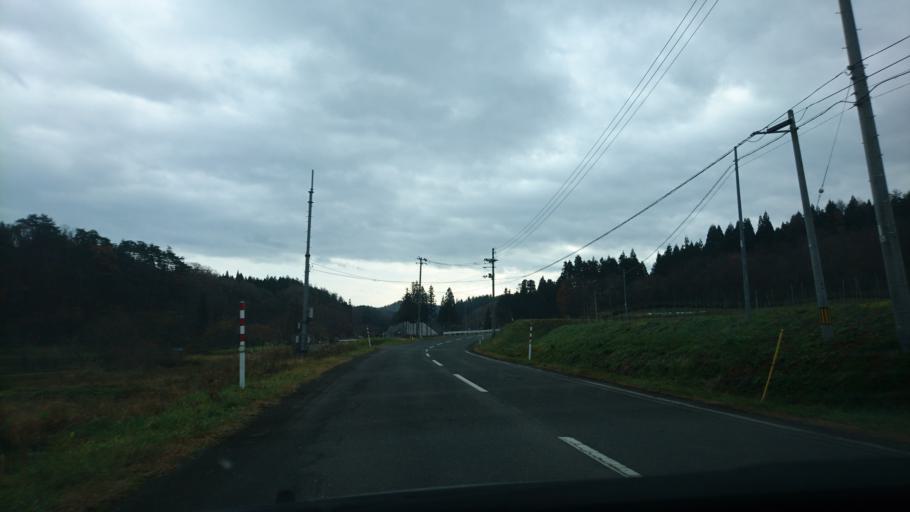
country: JP
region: Iwate
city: Ichinoseki
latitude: 38.9353
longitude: 140.9208
